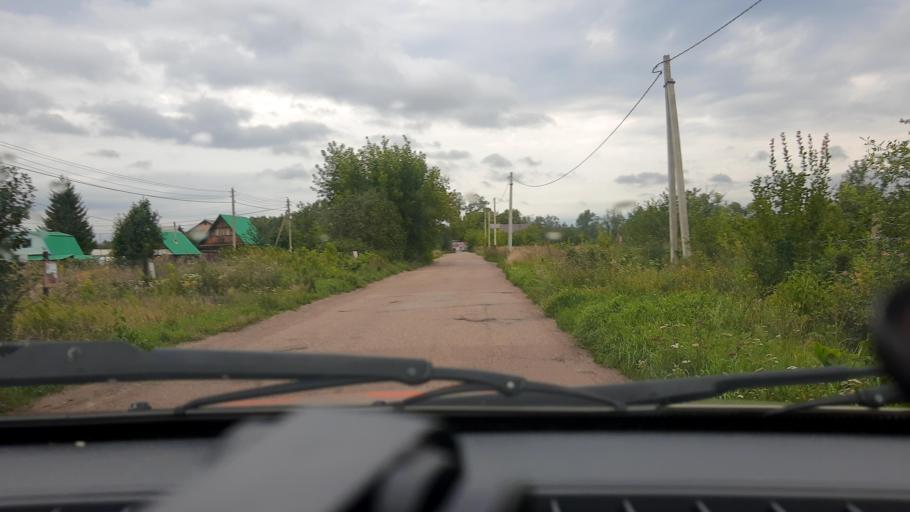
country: RU
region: Bashkortostan
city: Ufa
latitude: 54.5721
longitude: 55.8959
